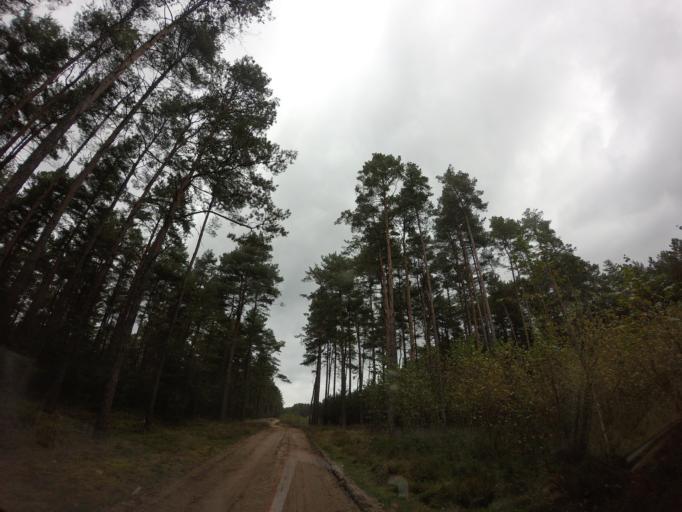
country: PL
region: West Pomeranian Voivodeship
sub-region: Powiat choszczenski
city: Drawno
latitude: 53.1669
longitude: 15.7535
